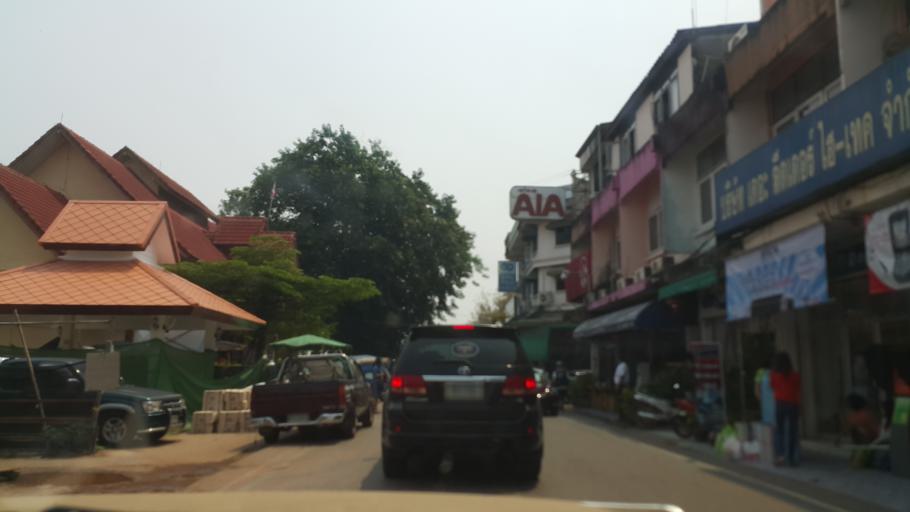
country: TH
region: Nakhon Phanom
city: Nakhon Phanom
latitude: 17.4033
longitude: 104.7881
